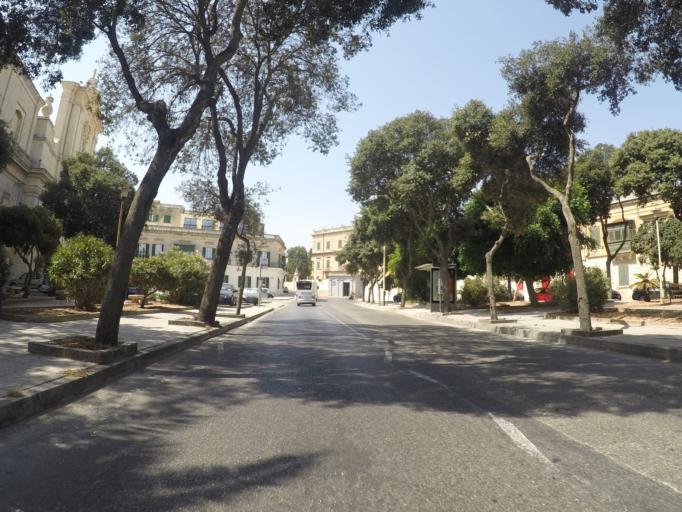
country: MT
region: Ir-Rabat
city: Rabat
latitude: 35.8765
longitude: 14.3991
